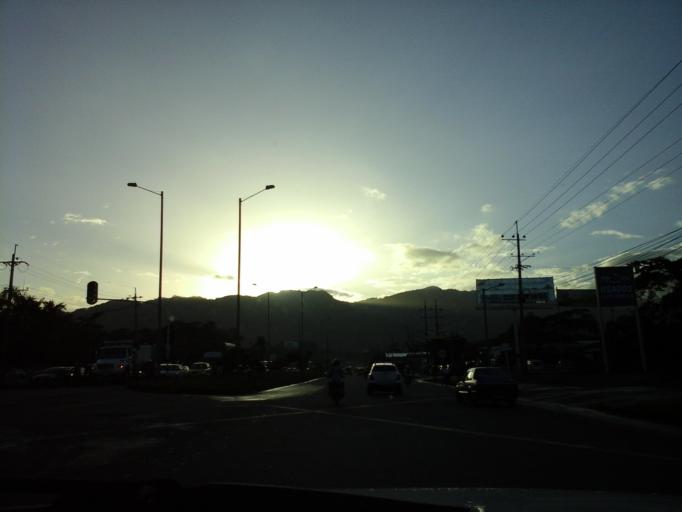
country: CO
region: Meta
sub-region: Villavicencio
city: Villavicencio
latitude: 4.1157
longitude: -73.6338
